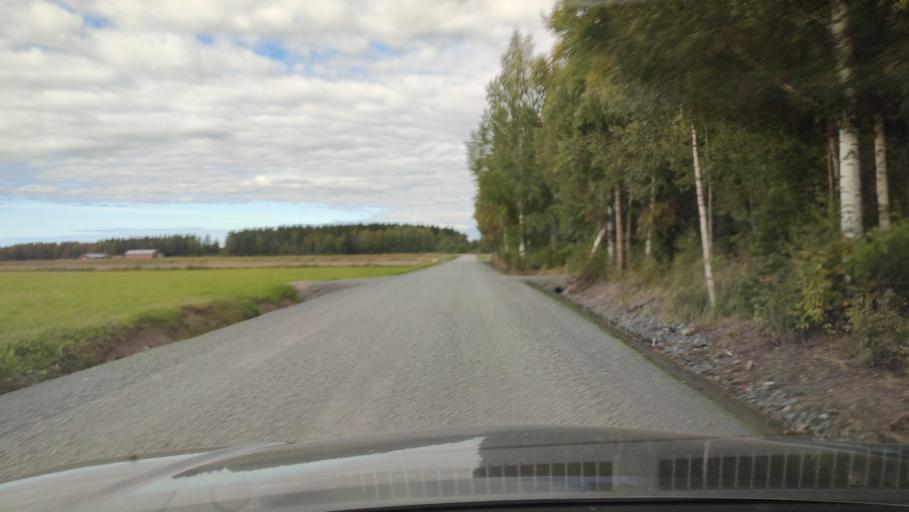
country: FI
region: Southern Ostrobothnia
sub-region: Suupohja
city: Karijoki
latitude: 62.2282
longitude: 21.6191
